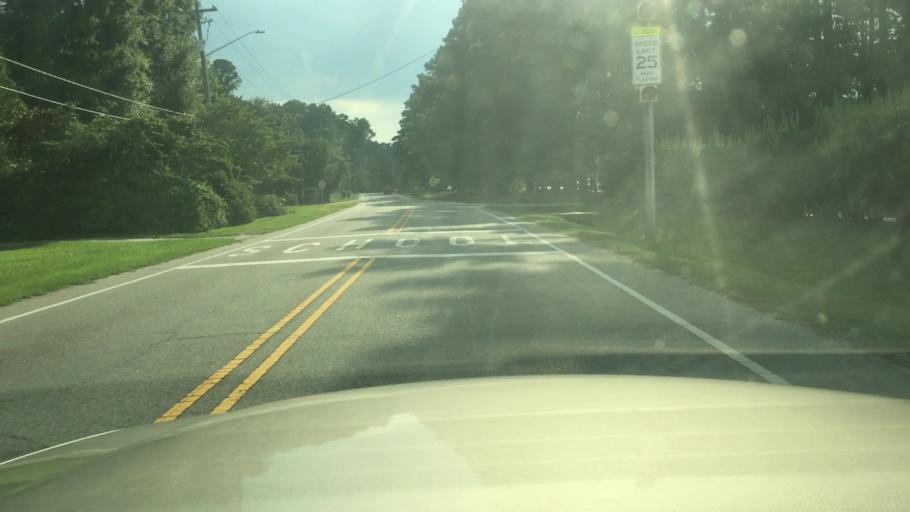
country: US
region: North Carolina
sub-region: Cumberland County
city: Fayetteville
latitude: 35.0623
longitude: -78.9386
